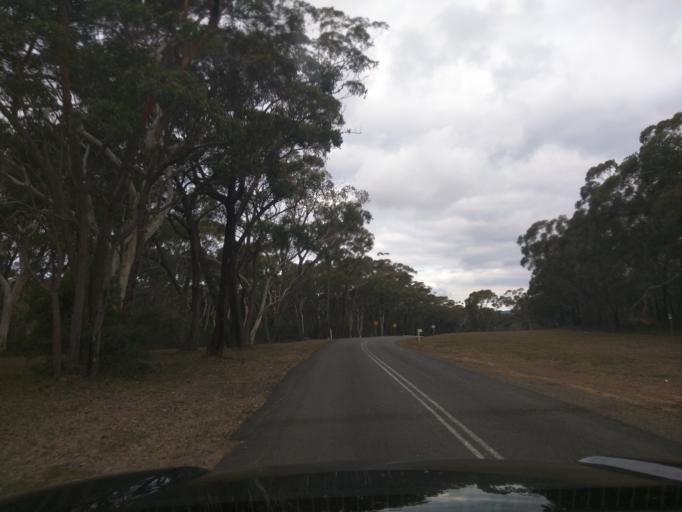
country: AU
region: New South Wales
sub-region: Wollondilly
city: Douglas Park
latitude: -34.3214
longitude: 150.7450
